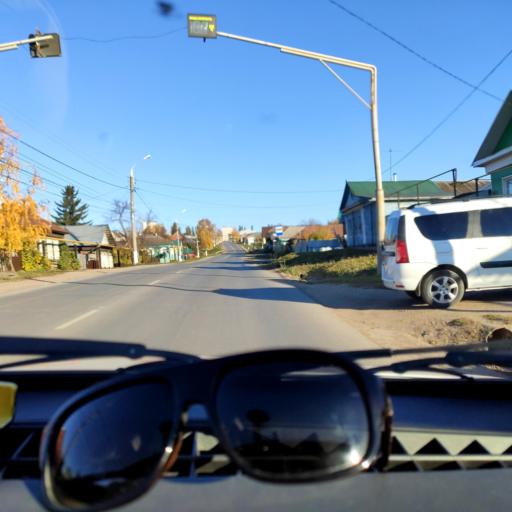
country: RU
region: Bashkortostan
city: Blagoveshchensk
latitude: 55.0396
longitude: 55.9624
